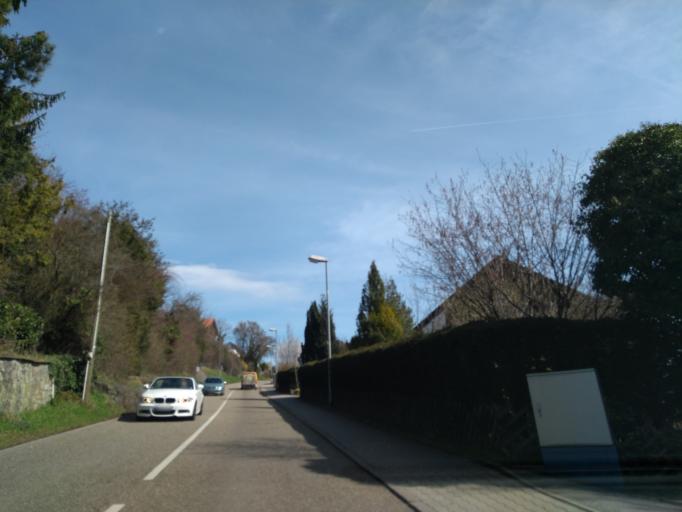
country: DE
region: Baden-Wuerttemberg
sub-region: Karlsruhe Region
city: Ispringen
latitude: 48.8939
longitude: 8.6705
